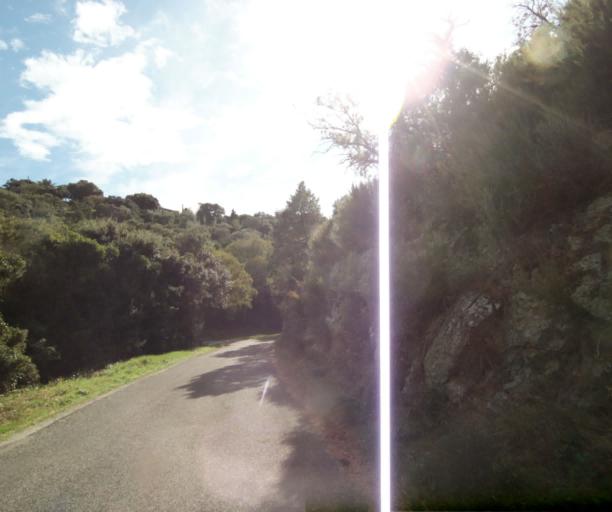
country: FR
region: Languedoc-Roussillon
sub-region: Departement des Pyrenees-Orientales
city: Sorede
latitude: 42.5233
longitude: 2.9870
